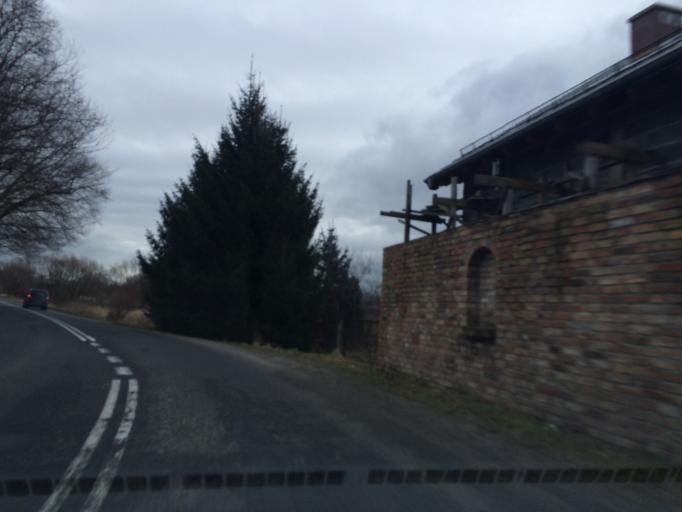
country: PL
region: Lower Silesian Voivodeship
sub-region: Powiat boleslawiecki
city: Nowogrodziec
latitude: 51.1730
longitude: 15.3377
